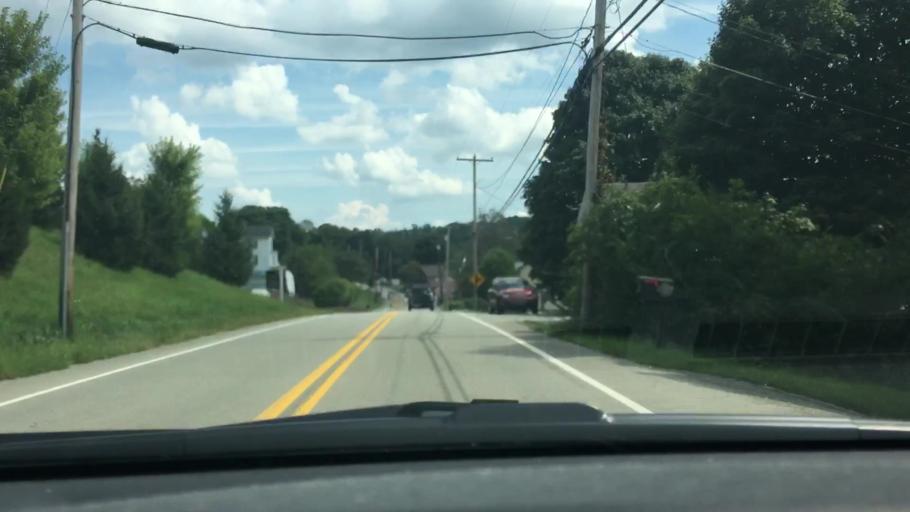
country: US
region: Pennsylvania
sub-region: Washington County
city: Gastonville
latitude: 40.2464
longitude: -80.0400
